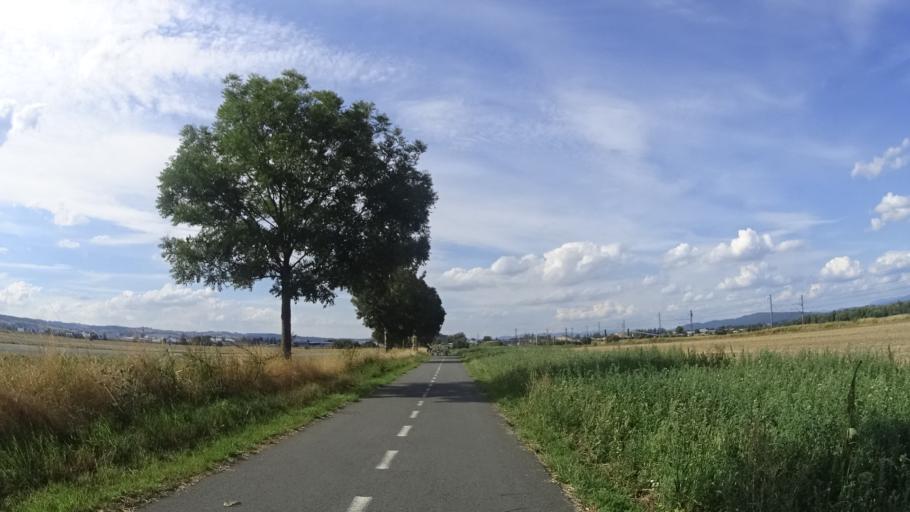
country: CZ
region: Olomoucky
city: Moravicany
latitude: 49.7643
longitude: 16.9498
